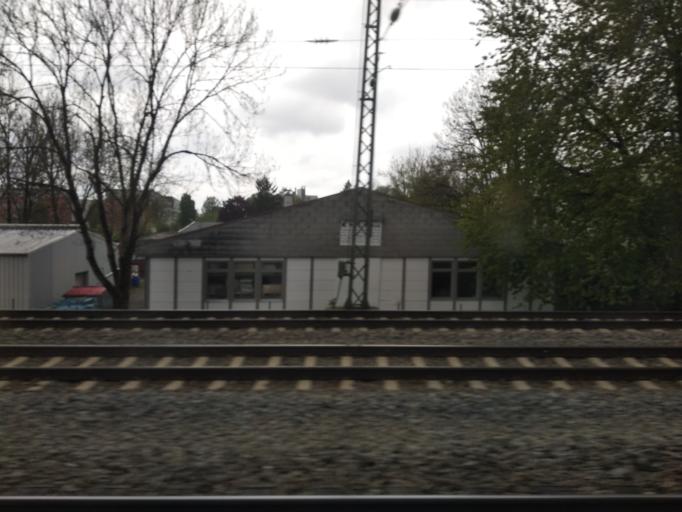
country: DE
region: Bavaria
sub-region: Upper Bavaria
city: Bogenhausen
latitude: 48.1306
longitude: 11.6517
